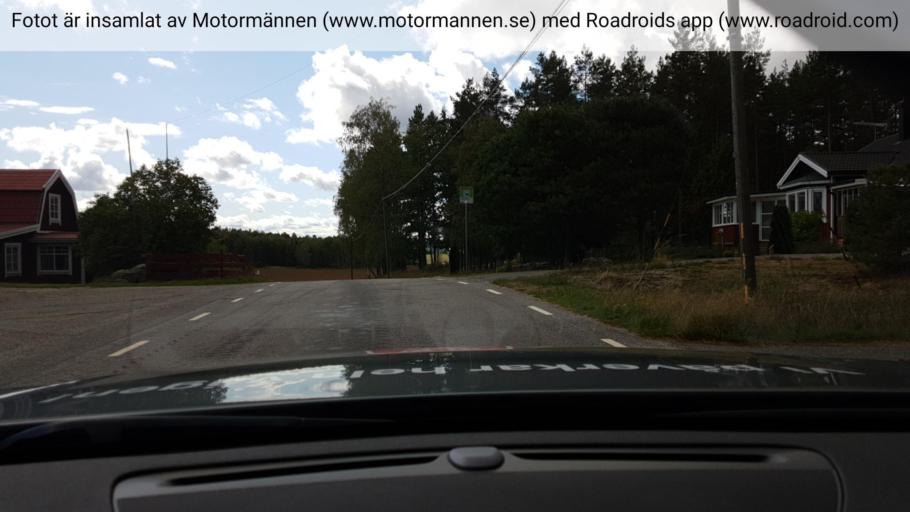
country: SE
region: Soedermanland
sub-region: Strangnas Kommun
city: Stallarholmen
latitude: 59.3905
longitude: 17.2671
